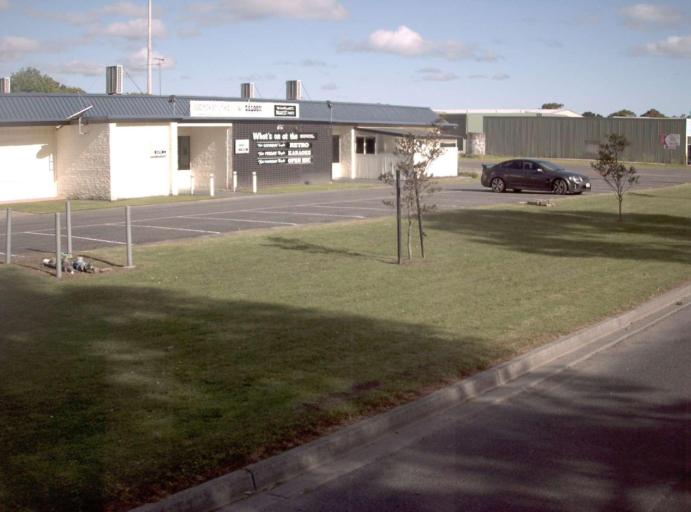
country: AU
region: Victoria
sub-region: Bass Coast
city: North Wonthaggi
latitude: -38.5953
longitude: 145.5920
